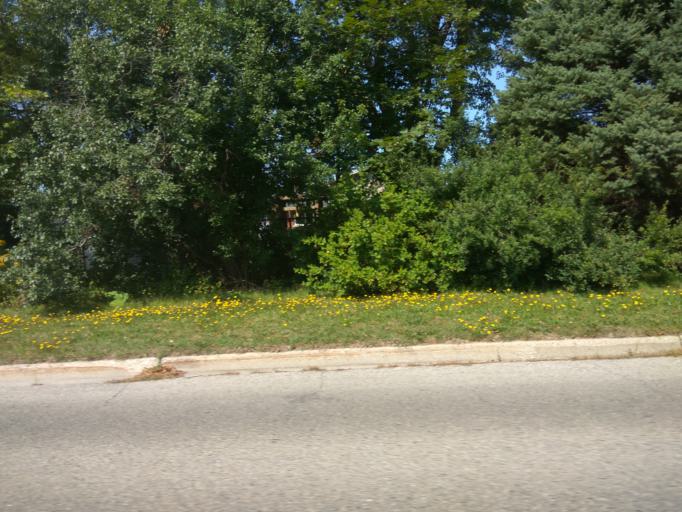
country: CA
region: Ontario
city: Stratford
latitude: 43.3839
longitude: -80.9689
